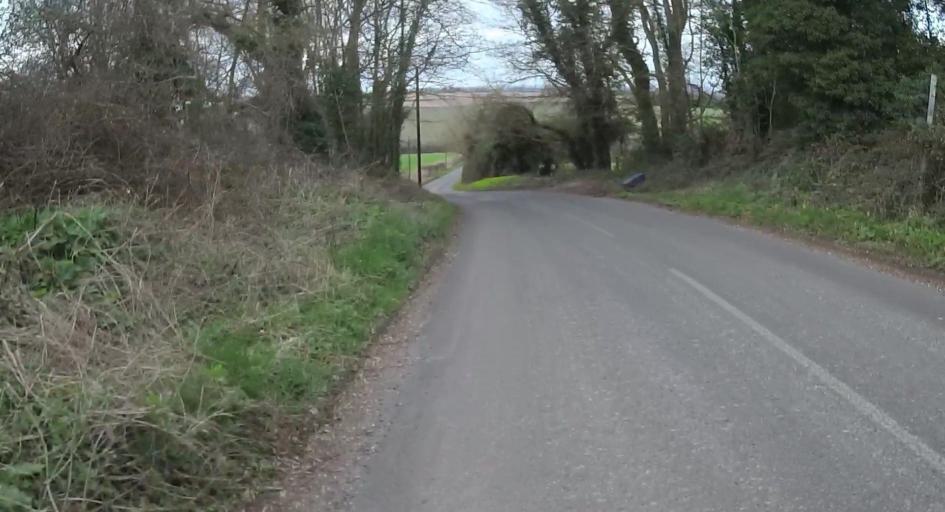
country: GB
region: England
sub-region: Hampshire
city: Abbotts Ann
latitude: 51.1472
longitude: -1.4867
